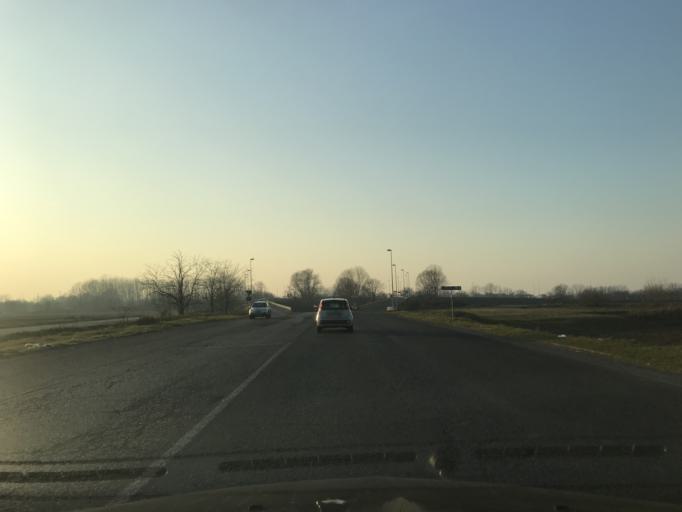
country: IT
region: Lombardy
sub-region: Provincia di Pavia
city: San Genesio ed Uniti
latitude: 45.2096
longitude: 9.1777
